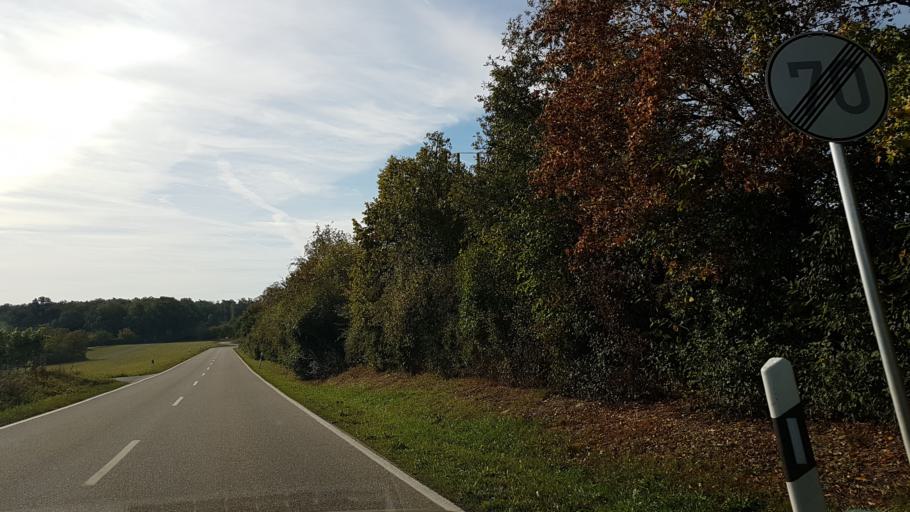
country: DE
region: Baden-Wuerttemberg
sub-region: Regierungsbezirk Stuttgart
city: Cleebronn
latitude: 49.0388
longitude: 9.0560
